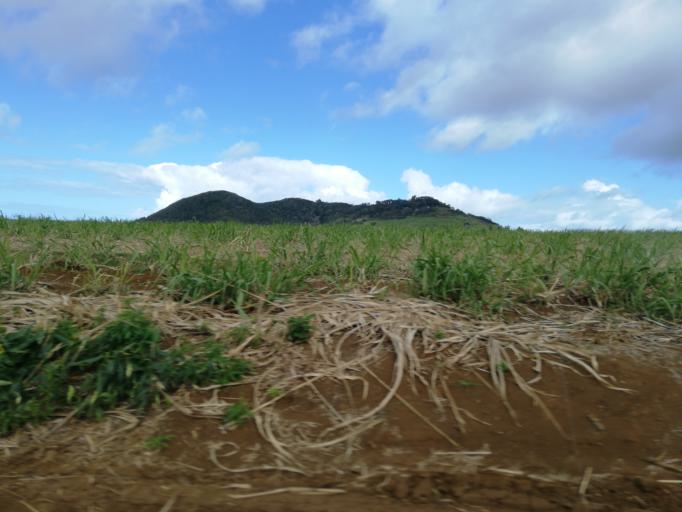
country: MU
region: Flacq
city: Grande Riviere Sud Est
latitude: -20.2824
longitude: 57.7563
